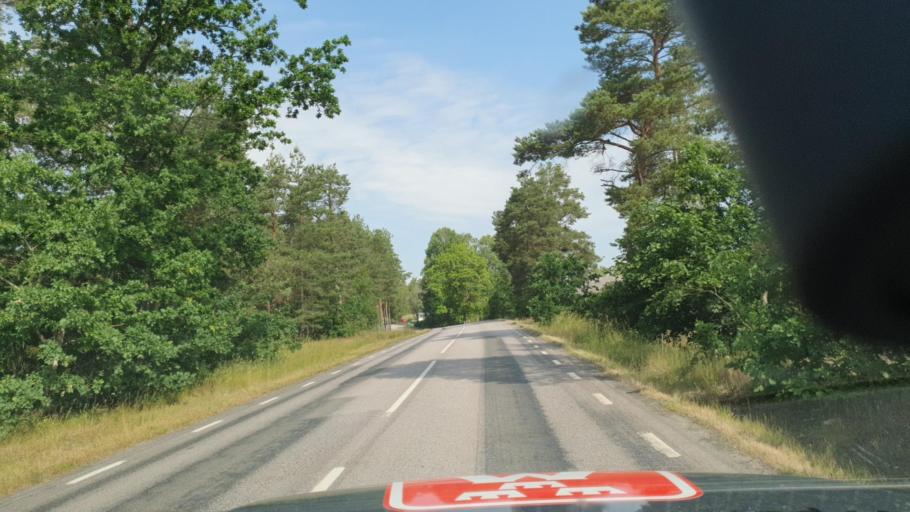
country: SE
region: Kalmar
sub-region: Kalmar Kommun
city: Ljungbyholm
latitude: 56.6712
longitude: 16.1559
